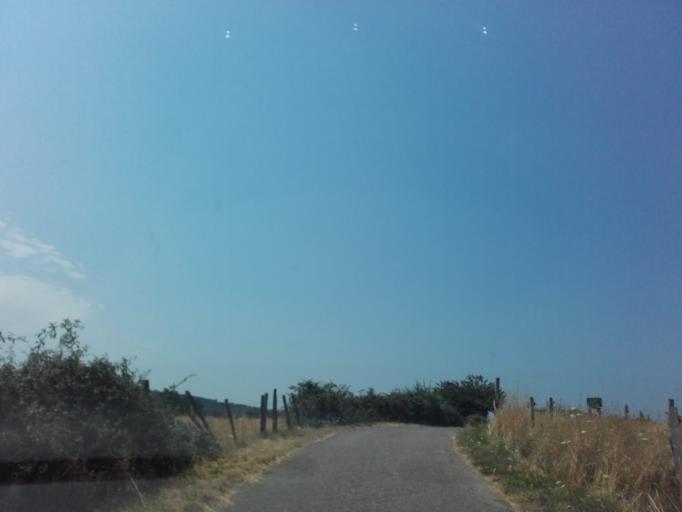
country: FR
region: Rhone-Alpes
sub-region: Departement de l'Isere
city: Saint-Simeon-de-Bressieux
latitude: 45.3194
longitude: 5.2590
